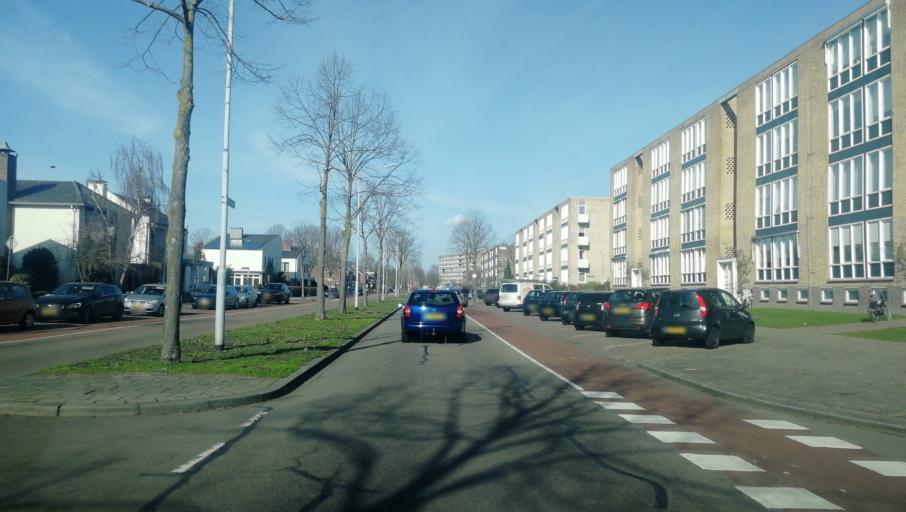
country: NL
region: Limburg
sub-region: Gemeente Venlo
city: Venlo
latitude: 51.3678
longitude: 6.1853
